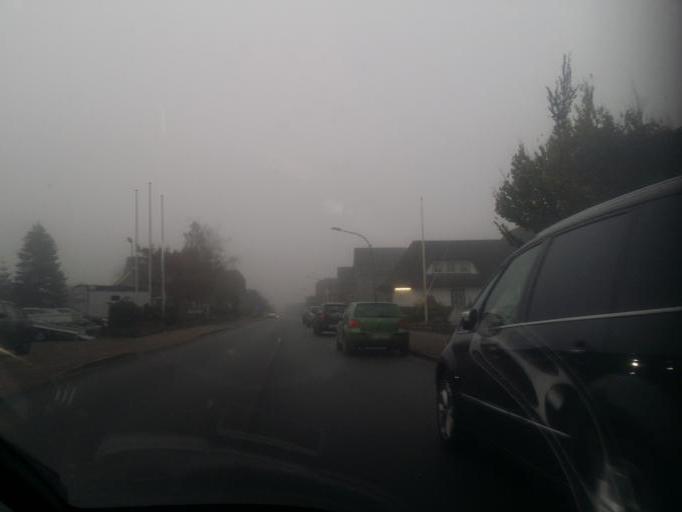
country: DE
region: Schleswig-Holstein
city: Viol
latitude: 54.5691
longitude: 9.1755
